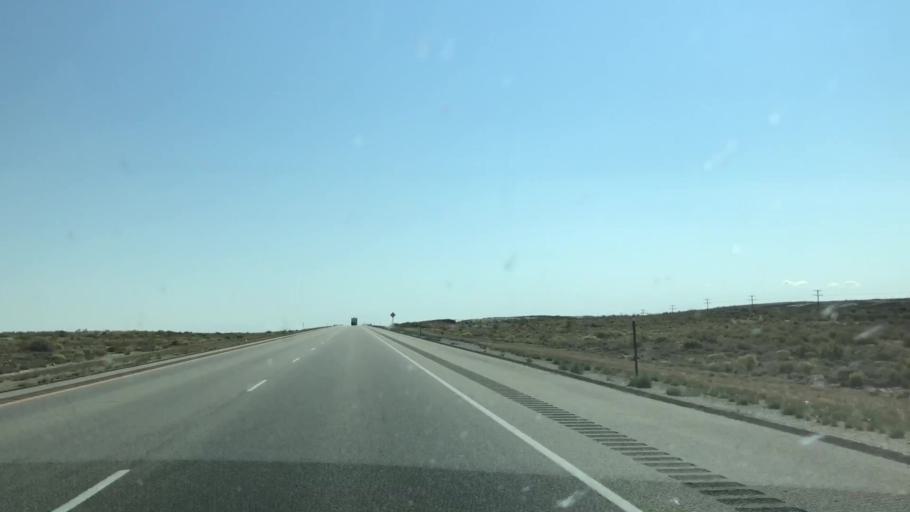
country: US
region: Wyoming
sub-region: Carbon County
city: Rawlins
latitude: 41.7042
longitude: -107.8558
